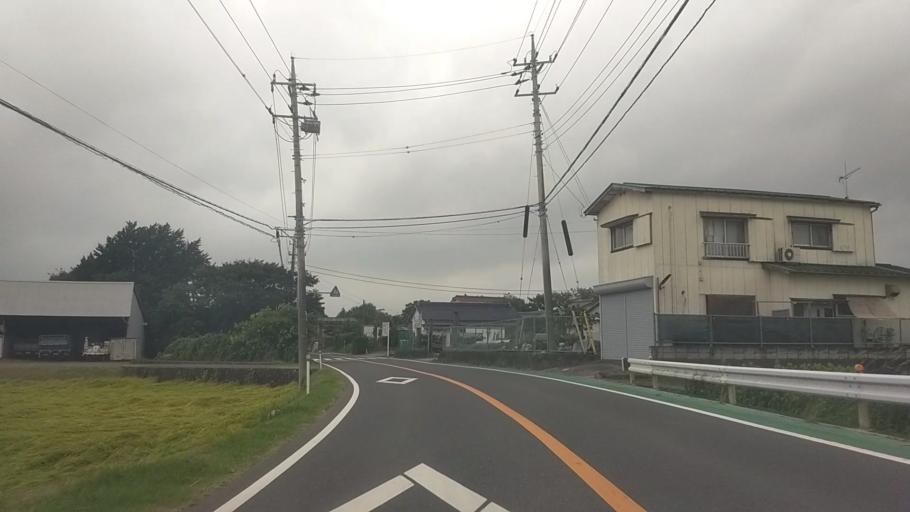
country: JP
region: Chiba
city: Kawaguchi
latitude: 35.1274
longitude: 140.0544
